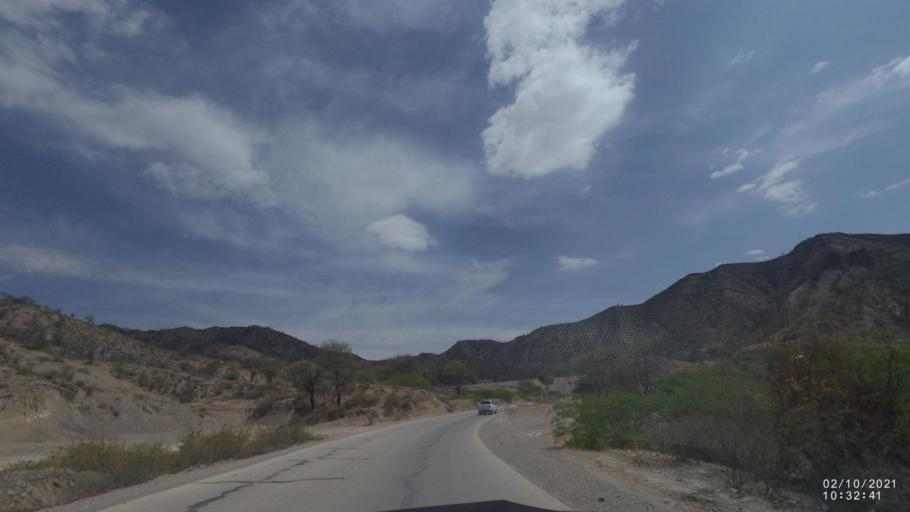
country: BO
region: Cochabamba
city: Capinota
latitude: -17.6862
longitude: -66.2595
